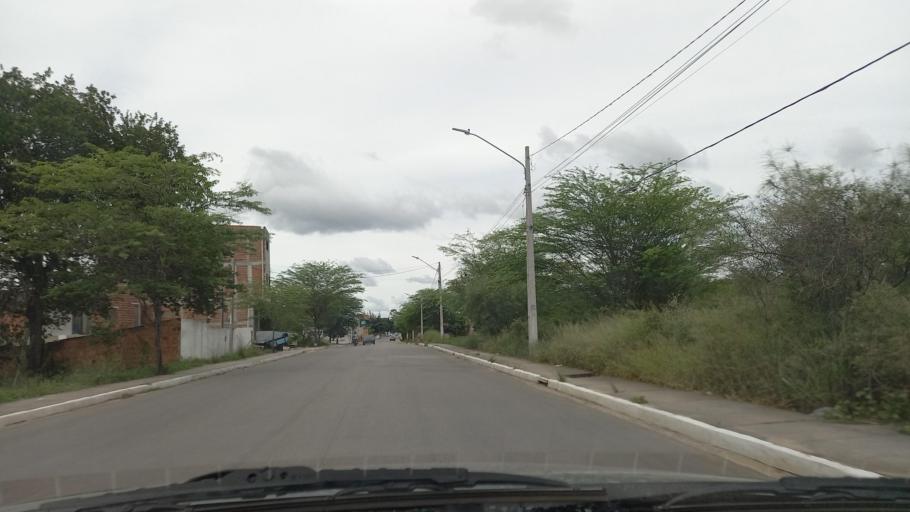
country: BR
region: Pernambuco
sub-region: Gravata
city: Gravata
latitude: -8.2083
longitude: -35.5910
